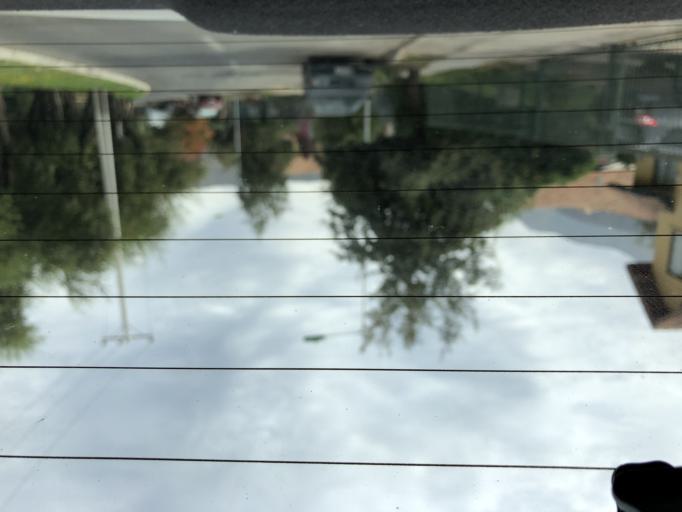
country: CL
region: Santiago Metropolitan
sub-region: Provincia de Cordillera
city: Puente Alto
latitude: -33.5835
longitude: -70.5123
